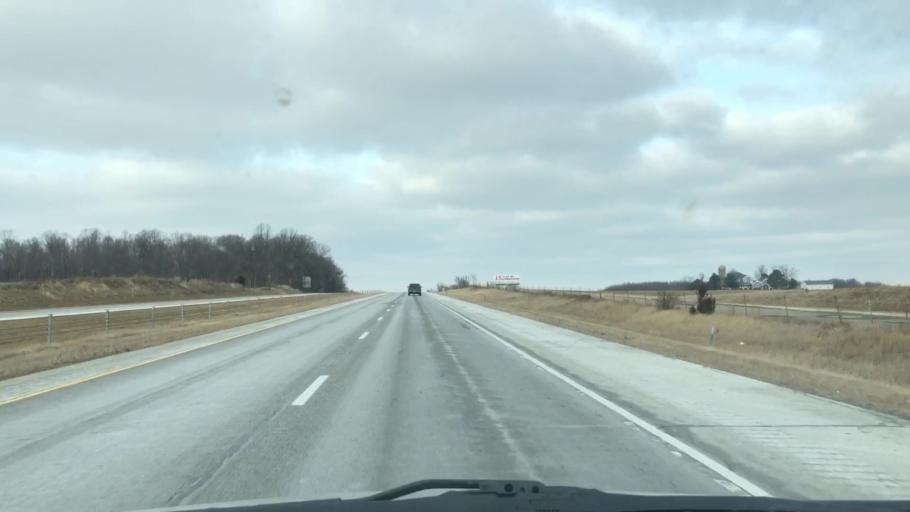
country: US
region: Indiana
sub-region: Steuben County
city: Angola
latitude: 41.5440
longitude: -85.0561
